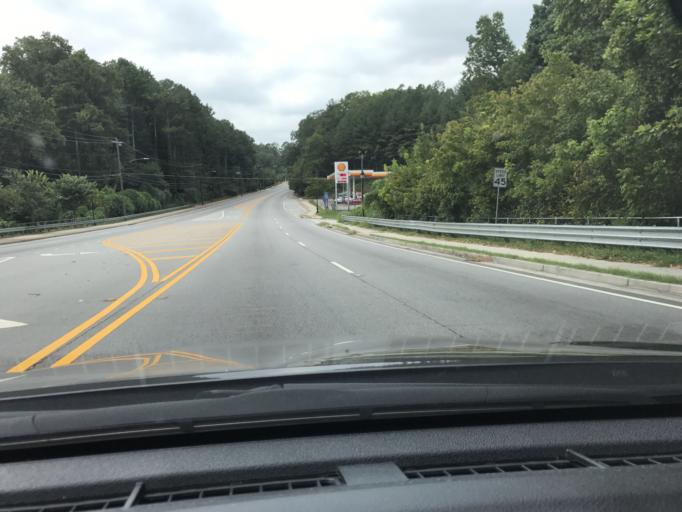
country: US
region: Georgia
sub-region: DeKalb County
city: Belvedere Park
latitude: 33.7483
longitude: -84.2804
